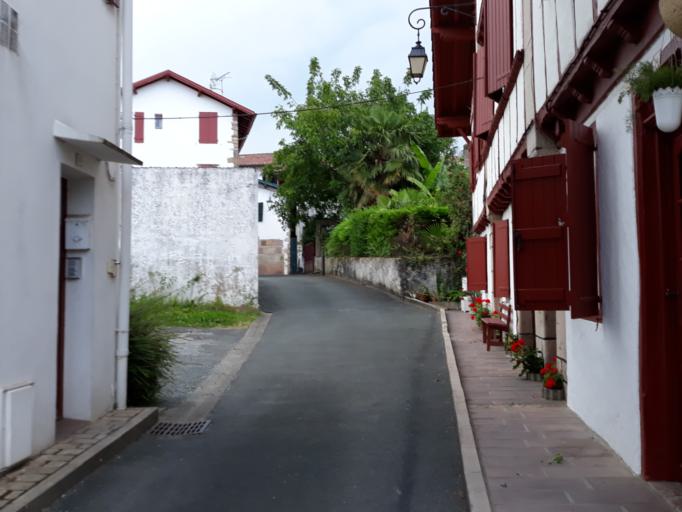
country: FR
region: Aquitaine
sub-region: Departement des Pyrenees-Atlantiques
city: Ascain
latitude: 43.3452
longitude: -1.6219
